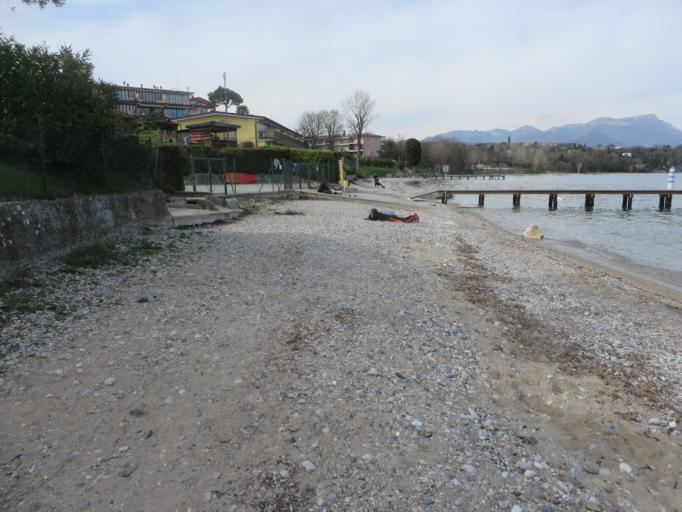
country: IT
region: Lombardy
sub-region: Provincia di Brescia
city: Manerba del Garda
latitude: 45.5329
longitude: 10.5573
